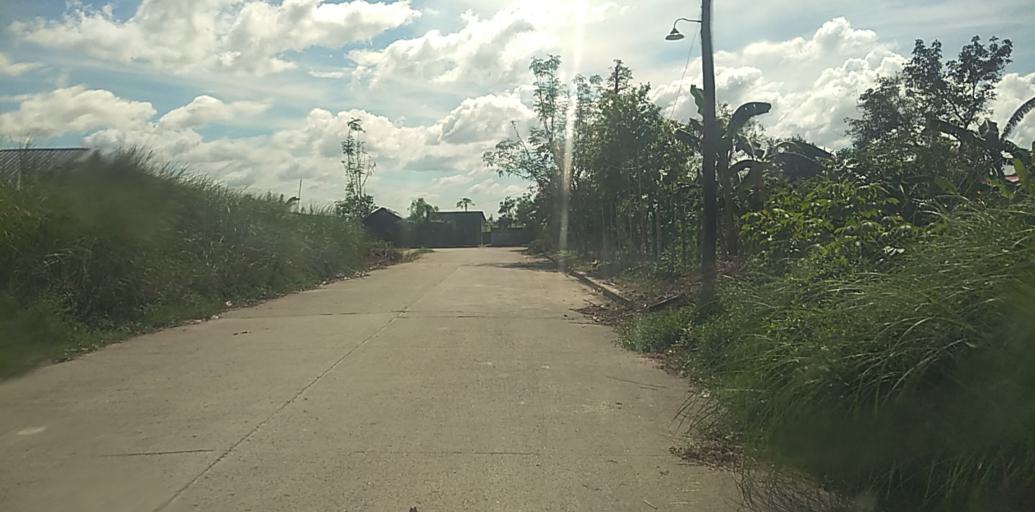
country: PH
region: Central Luzon
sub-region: Province of Pampanga
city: Buensuseso
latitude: 15.1887
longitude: 120.6633
